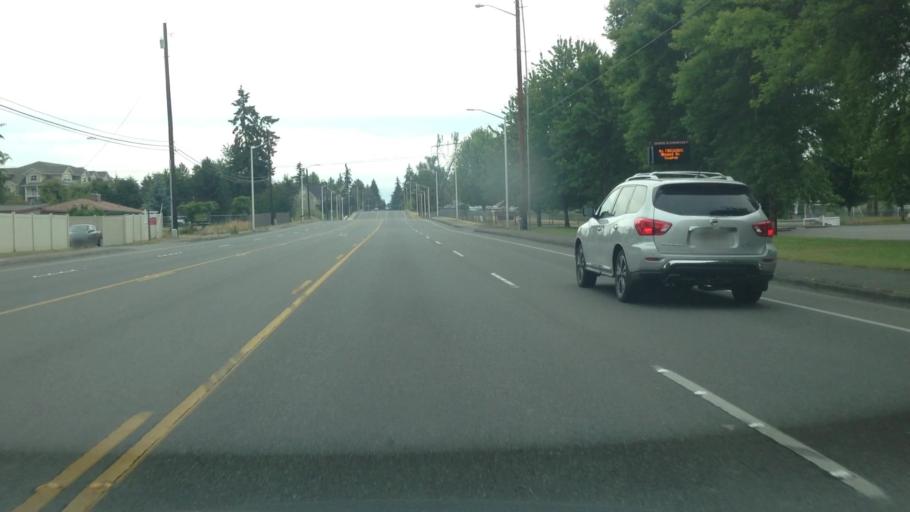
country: US
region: Washington
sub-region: Pierce County
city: South Hill
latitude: 47.1389
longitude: -122.3041
